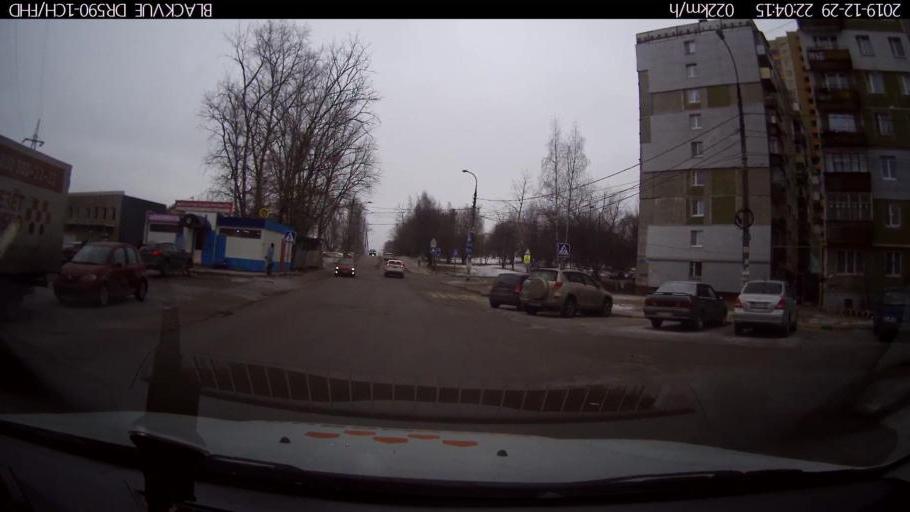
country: RU
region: Nizjnij Novgorod
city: Nizhniy Novgorod
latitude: 56.2286
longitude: 43.9484
